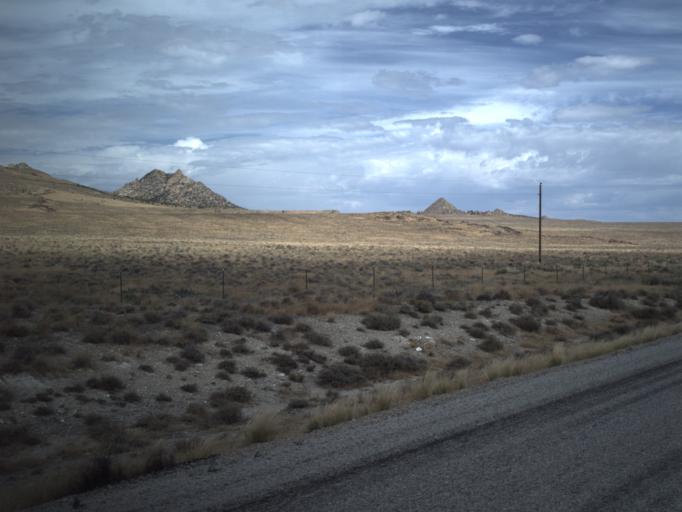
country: US
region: Utah
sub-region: Tooele County
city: Wendover
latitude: 41.4633
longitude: -113.6488
